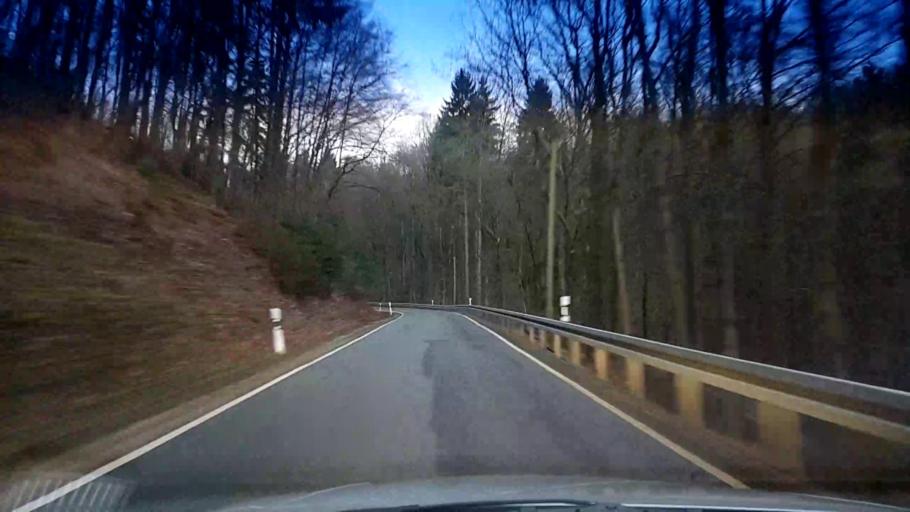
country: DE
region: Bavaria
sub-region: Upper Franconia
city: Wattendorf
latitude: 50.0502
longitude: 11.0601
